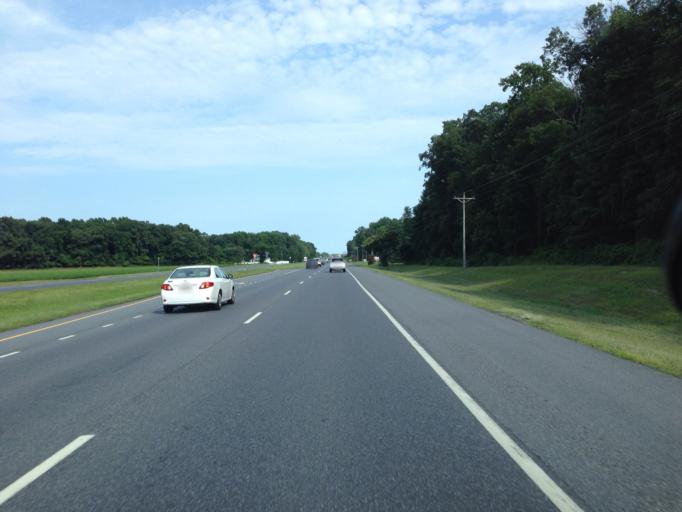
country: US
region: Delaware
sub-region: Sussex County
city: Milton
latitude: 38.8134
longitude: -75.2915
